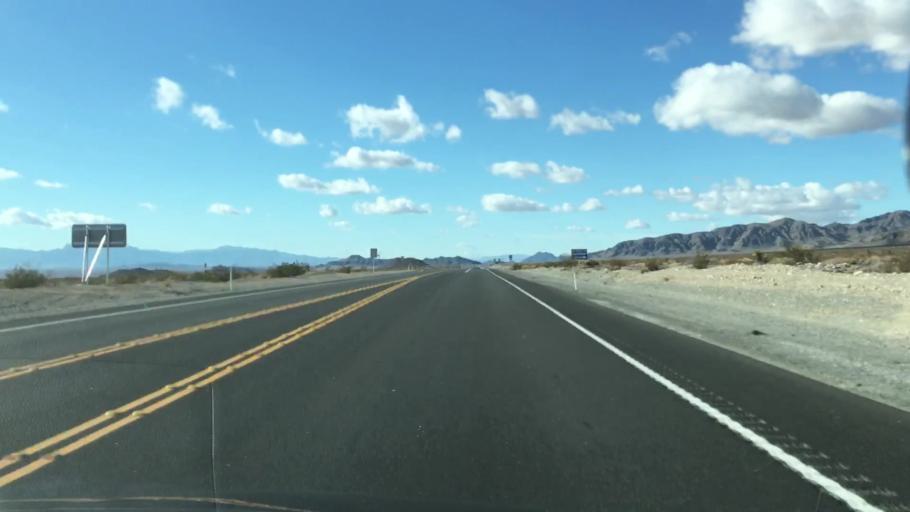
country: US
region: Nevada
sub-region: Nye County
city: Pahrump
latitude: 36.5645
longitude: -116.1209
